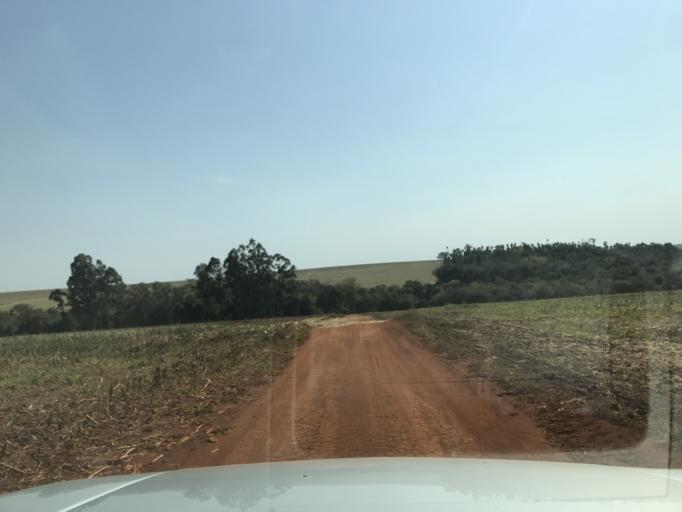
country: BR
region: Parana
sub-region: Palotina
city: Palotina
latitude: -24.2247
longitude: -53.7385
